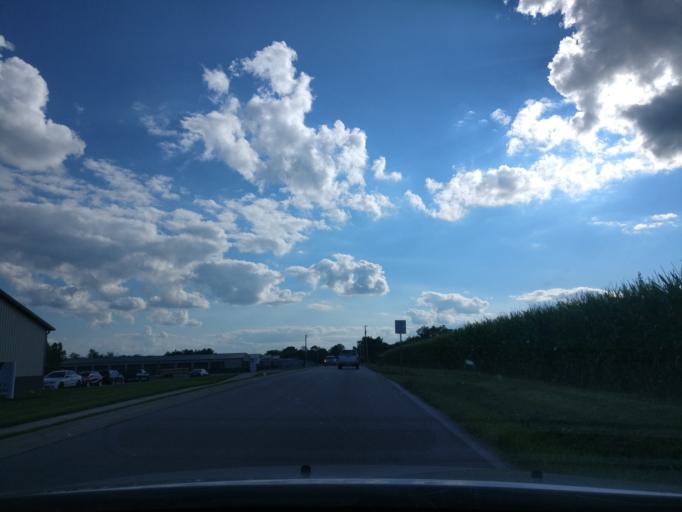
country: US
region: Ohio
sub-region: Clinton County
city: Wilmington
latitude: 39.4567
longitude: -83.8120
